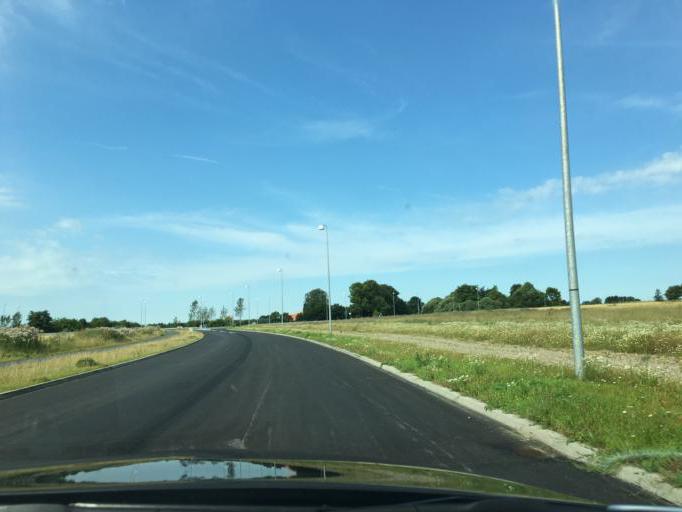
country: DK
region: South Denmark
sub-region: Kolding Kommune
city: Kolding
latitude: 55.5449
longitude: 9.4501
